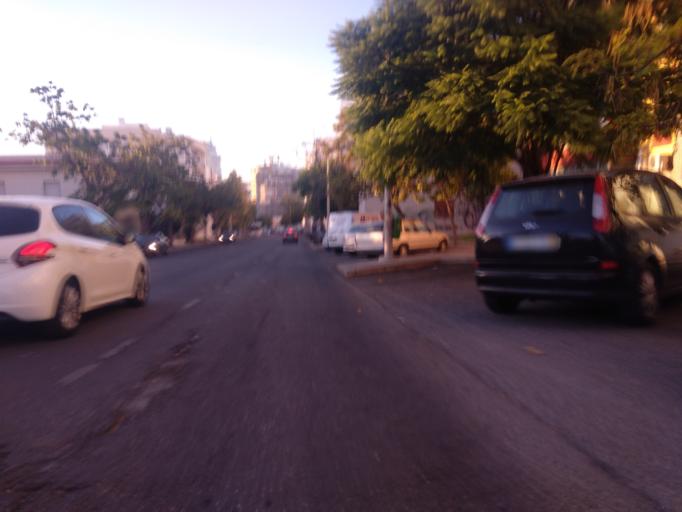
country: PT
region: Faro
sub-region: Faro
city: Faro
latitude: 37.0215
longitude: -7.9241
